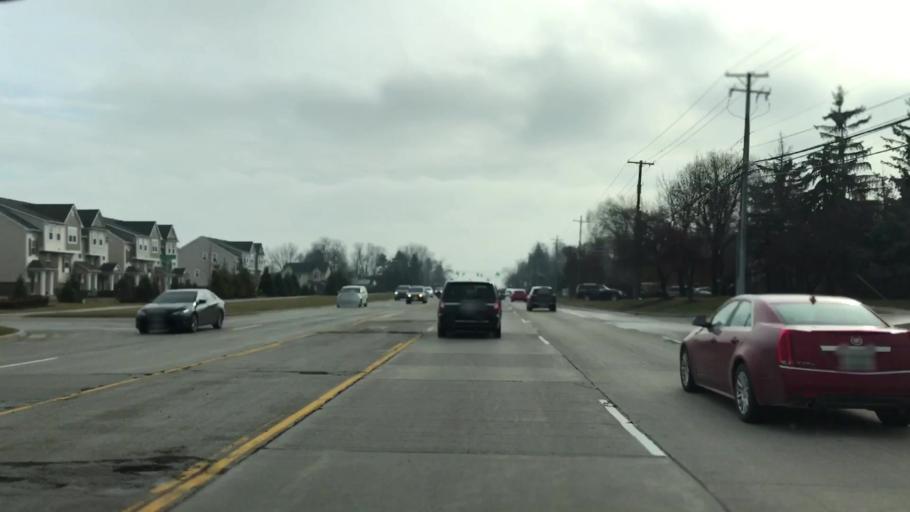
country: US
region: Michigan
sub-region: Oakland County
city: Troy
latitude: 42.5879
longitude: -83.1289
